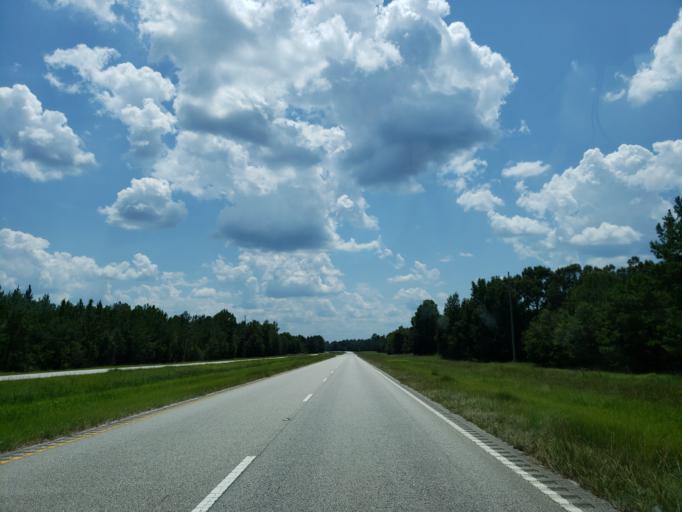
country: US
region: Mississippi
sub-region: Greene County
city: Leakesville
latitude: 31.2801
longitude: -88.5083
